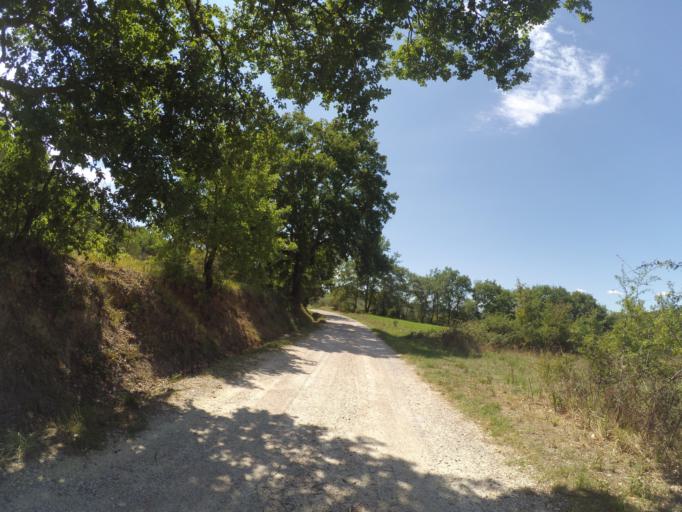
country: IT
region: Tuscany
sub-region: Province of Arezzo
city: Castiglion Fibocchi
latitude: 43.5364
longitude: 11.7663
